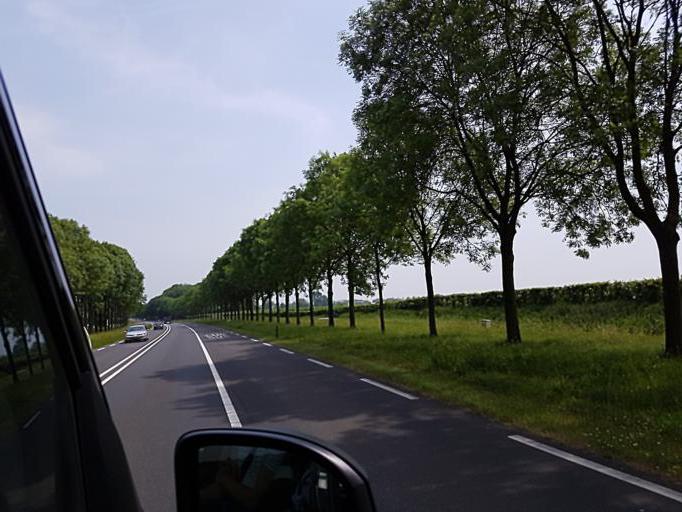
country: NL
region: Utrecht
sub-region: Gemeente Utrecht
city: Lunetten
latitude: 52.0440
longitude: 5.1317
